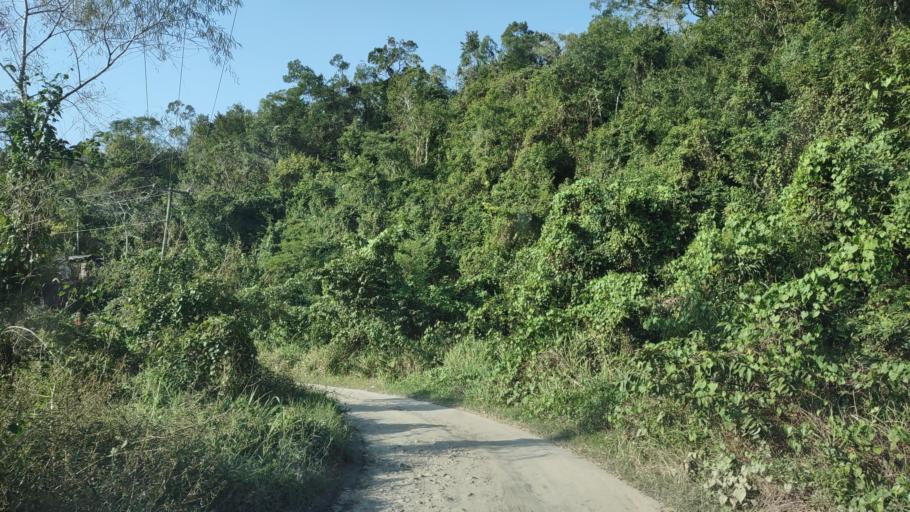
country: MX
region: Veracruz
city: Papantla de Olarte
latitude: 20.4607
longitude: -97.3618
